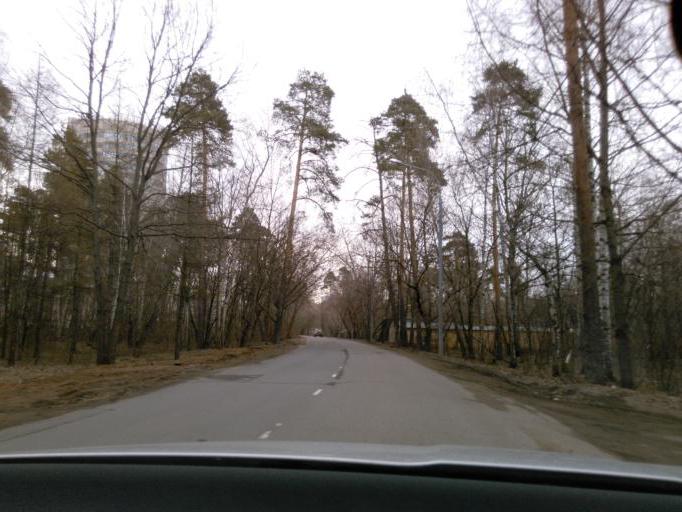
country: RU
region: Moskovskaya
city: Levoberezhnyy
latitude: 55.8265
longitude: 37.4857
